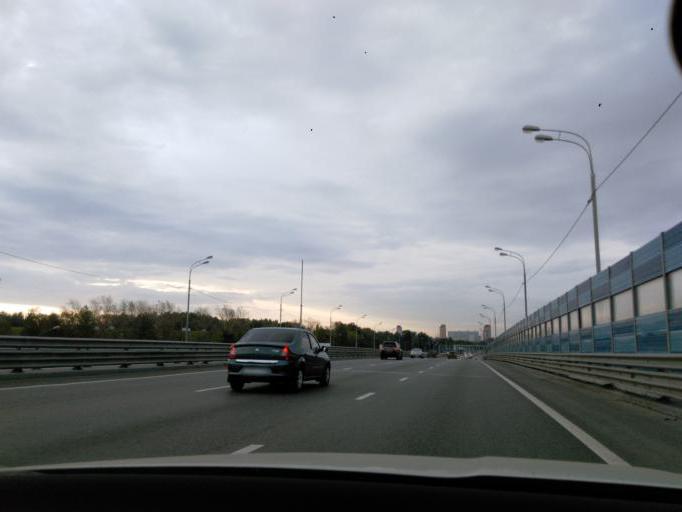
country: RU
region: Moscow
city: Severnyy
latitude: 55.9491
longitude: 37.5395
